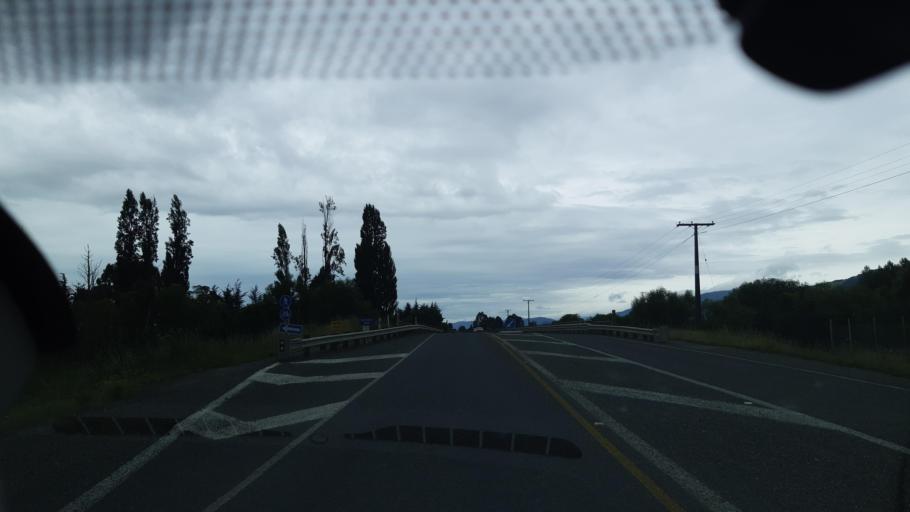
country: NZ
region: Tasman
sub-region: Tasman District
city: Brightwater
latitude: -41.3765
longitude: 173.1184
